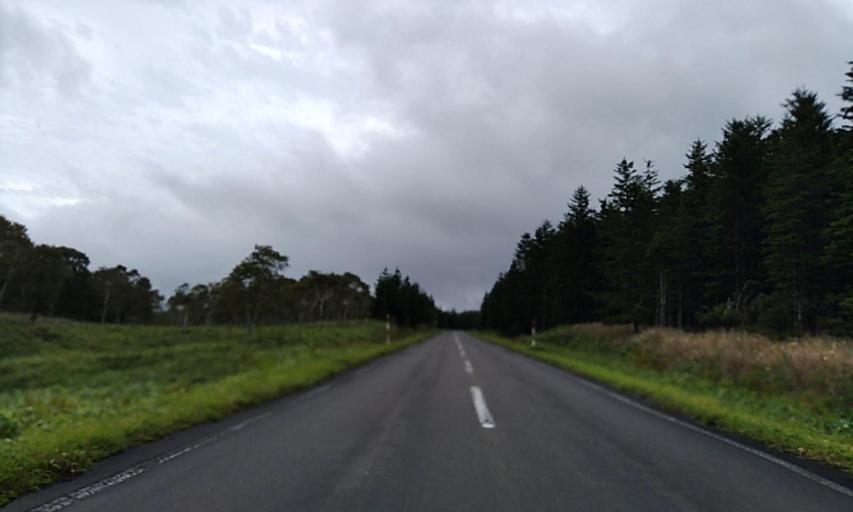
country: JP
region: Hokkaido
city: Abashiri
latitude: 43.6128
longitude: 144.5904
